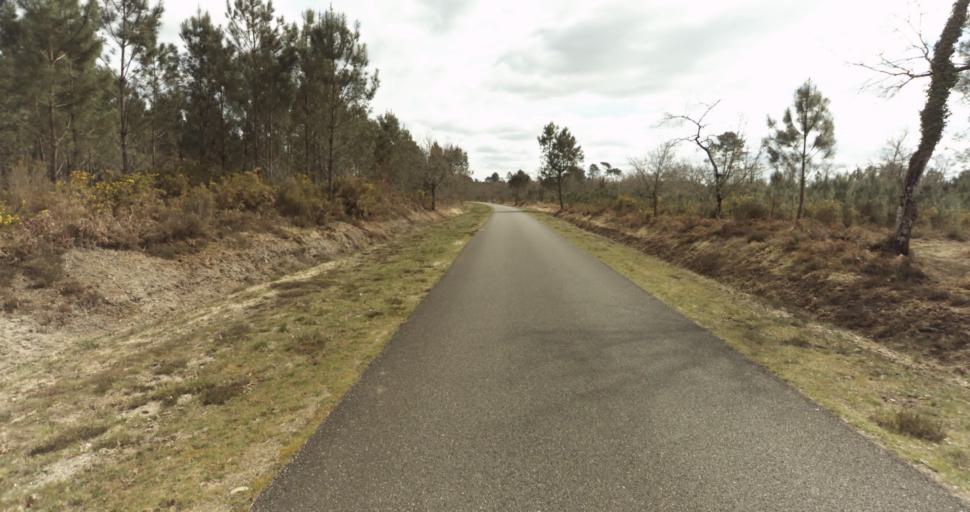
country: FR
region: Aquitaine
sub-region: Departement des Landes
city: Roquefort
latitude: 44.1065
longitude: -0.4482
